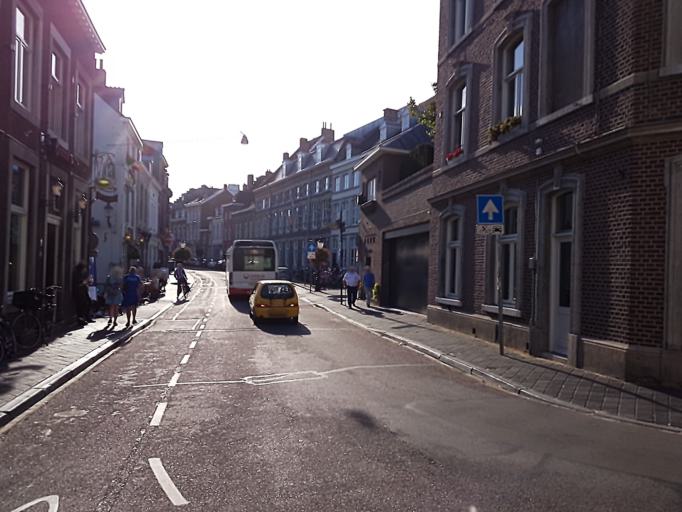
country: NL
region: Limburg
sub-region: Gemeente Maastricht
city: Maastricht
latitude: 50.8466
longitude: 5.6877
